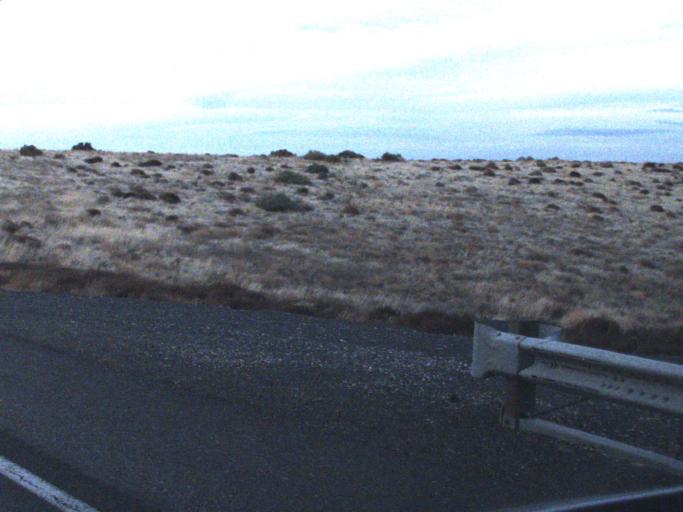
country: US
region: Washington
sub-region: Benton County
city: Finley
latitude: 46.0546
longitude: -118.8932
